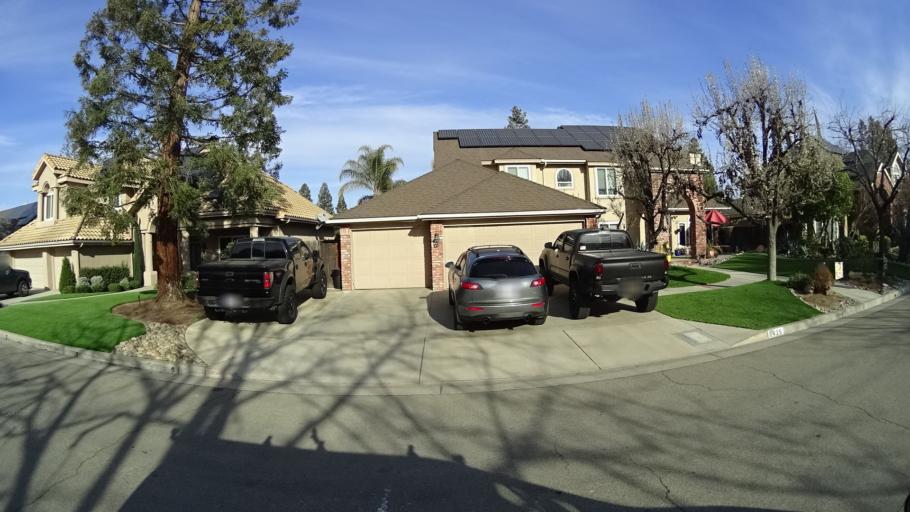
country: US
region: California
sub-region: Fresno County
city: Clovis
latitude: 36.8728
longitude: -119.7718
